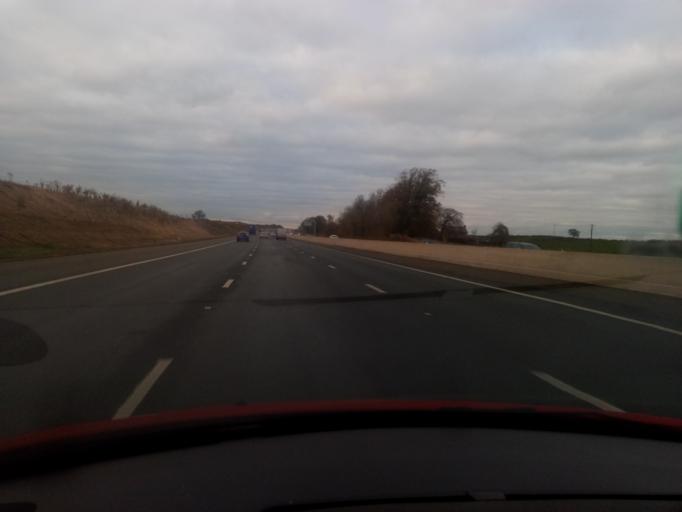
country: GB
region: England
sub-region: North Yorkshire
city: Bedale
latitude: 54.3304
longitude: -1.5868
